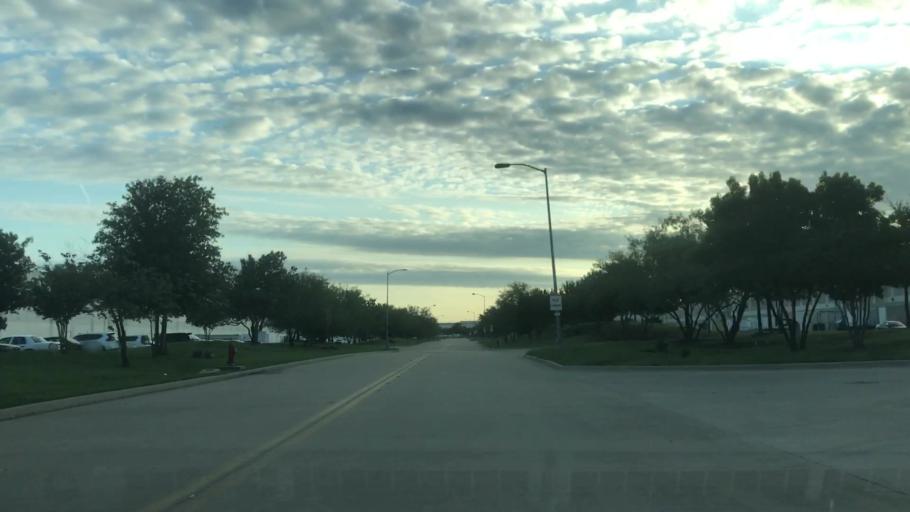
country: US
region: Texas
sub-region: Dallas County
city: Coppell
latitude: 32.9369
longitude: -97.0287
